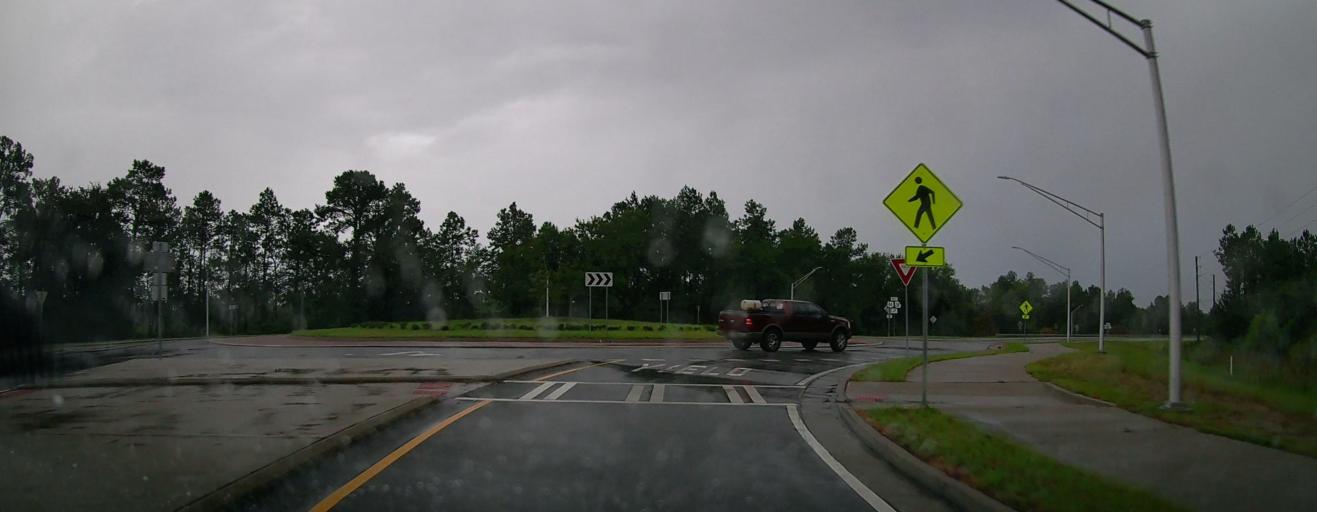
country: US
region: Georgia
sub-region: Clinch County
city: Homerville
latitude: 31.0678
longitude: -82.6668
